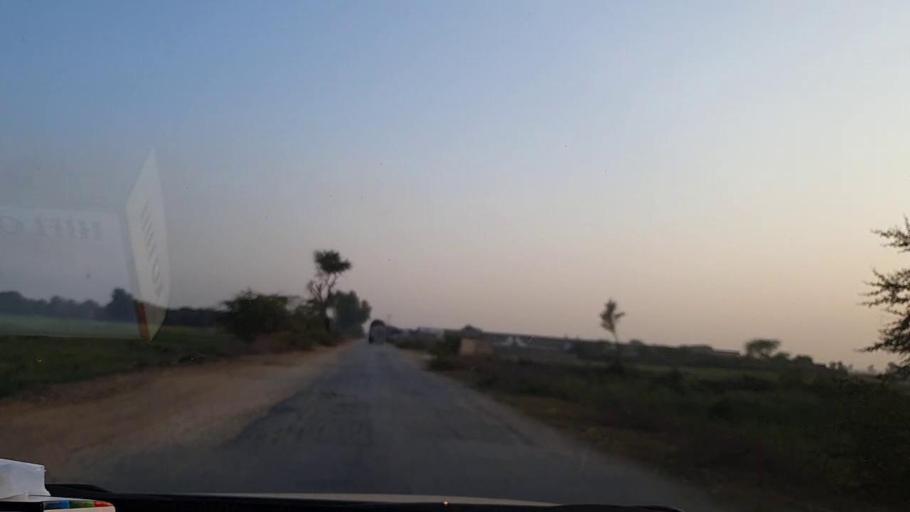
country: PK
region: Sindh
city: Tando Ghulam Ali
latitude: 25.1752
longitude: 68.9490
